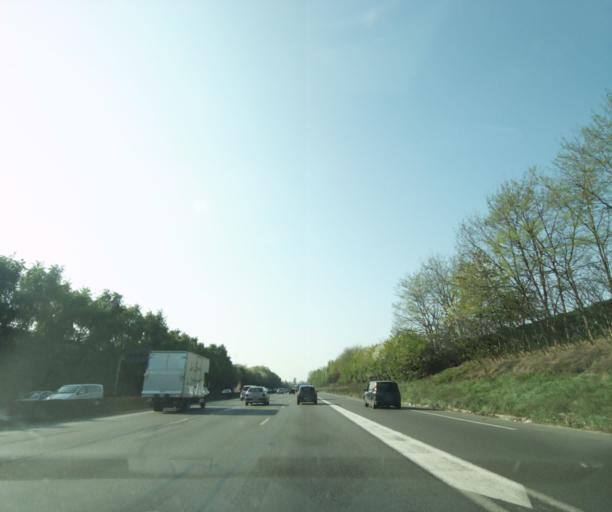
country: FR
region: Ile-de-France
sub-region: Departement de l'Essonne
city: Morsang-sur-Orge
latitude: 48.6622
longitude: 2.3691
